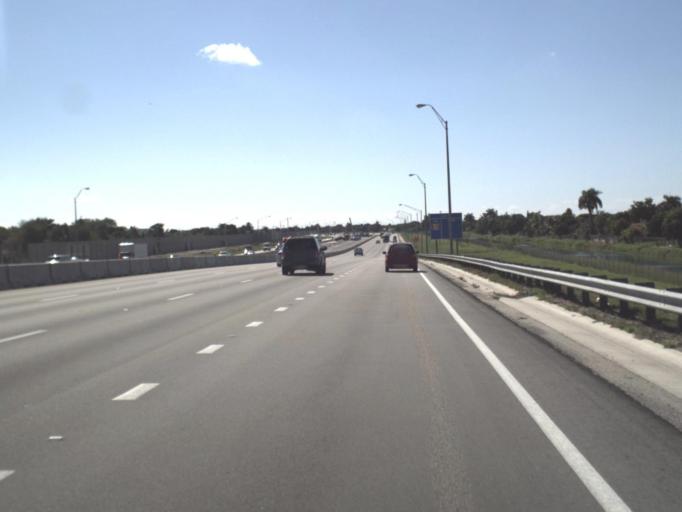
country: US
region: Florida
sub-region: Miami-Dade County
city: South Miami Heights
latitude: 25.6115
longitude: -80.3786
